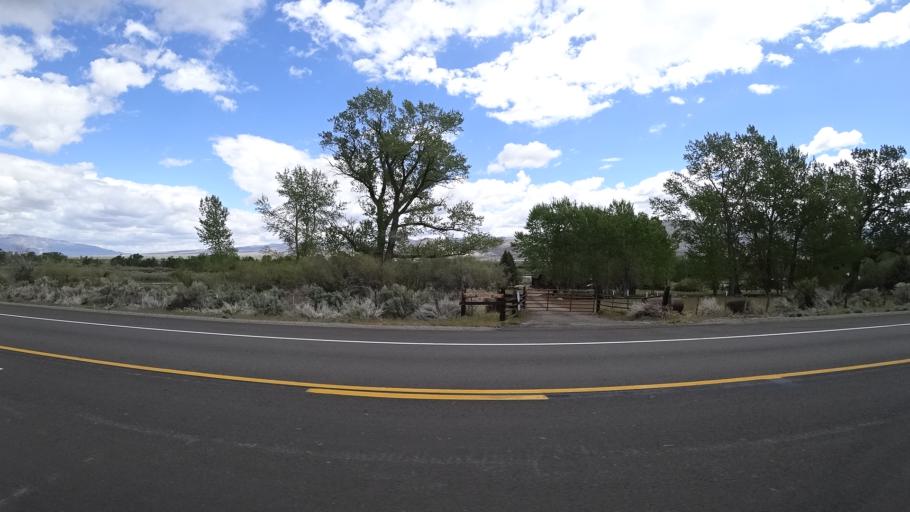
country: US
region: Nevada
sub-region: Lyon County
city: Smith Valley
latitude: 38.5704
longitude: -119.5094
